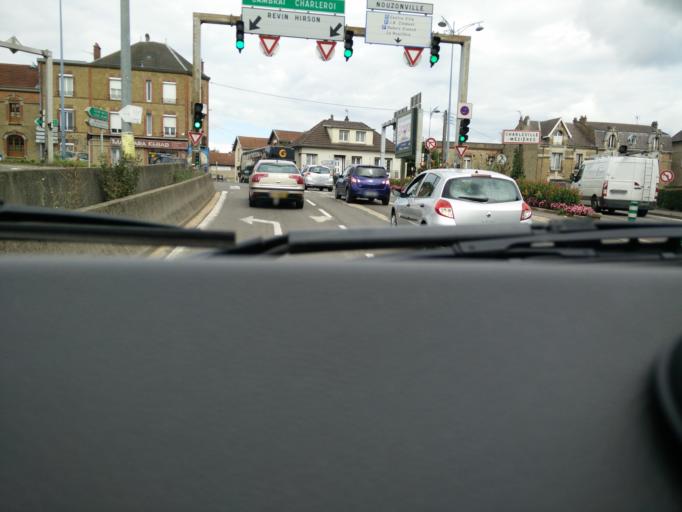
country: FR
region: Champagne-Ardenne
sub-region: Departement des Ardennes
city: Charleville-Mezieres
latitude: 49.7701
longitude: 4.7109
